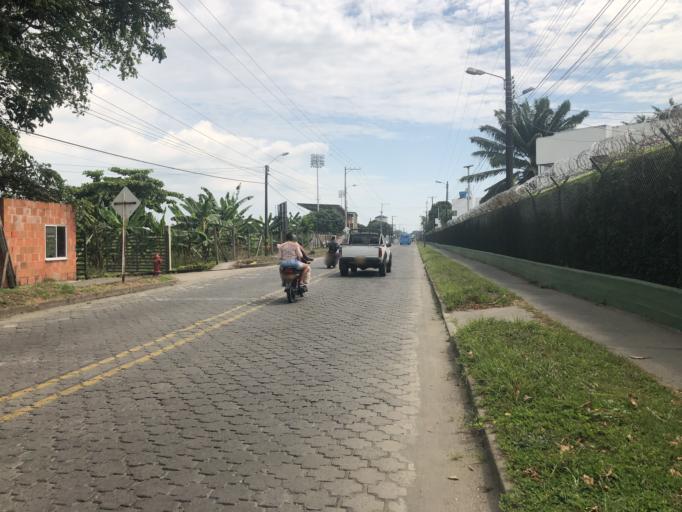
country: CO
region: Narino
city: Tumaco
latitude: 1.8218
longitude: -78.7449
